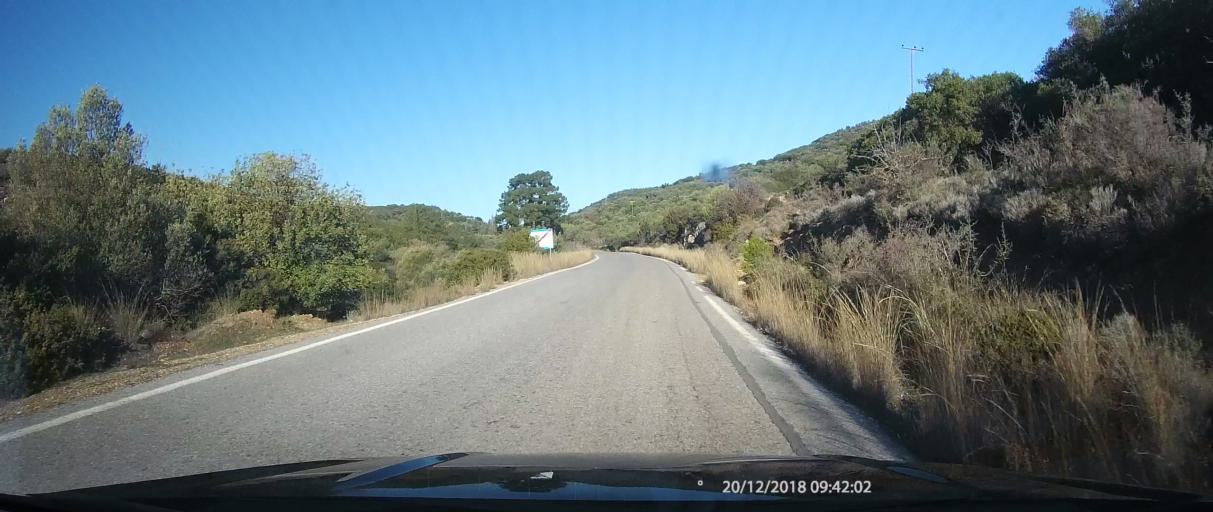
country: GR
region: Peloponnese
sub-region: Nomos Lakonias
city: Yerakion
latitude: 36.9553
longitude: 22.7591
